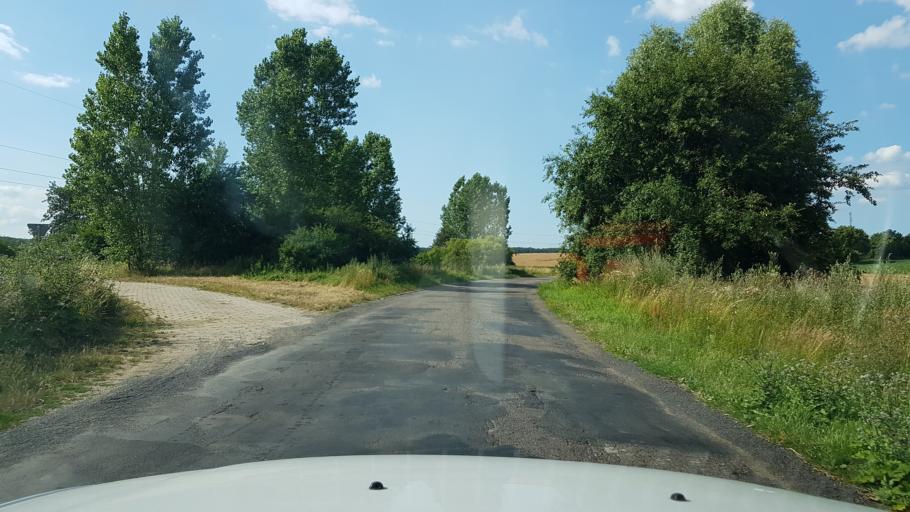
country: PL
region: West Pomeranian Voivodeship
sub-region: Powiat gryfinski
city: Stare Czarnowo
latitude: 53.2951
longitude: 14.8042
